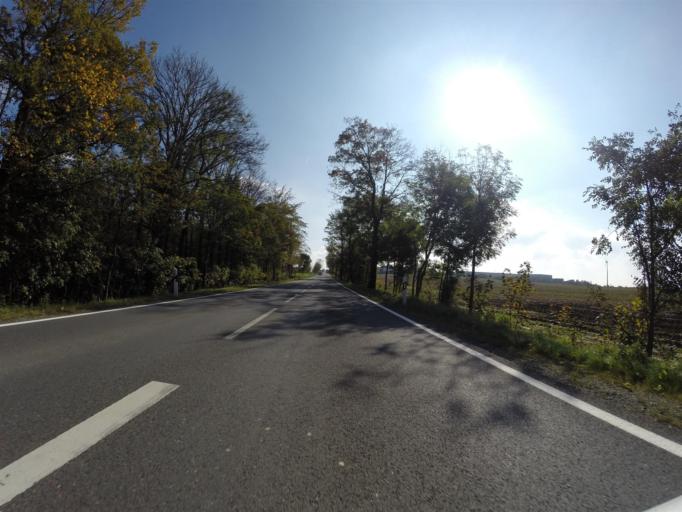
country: DE
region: Thuringia
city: Tanna
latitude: 50.5005
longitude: 11.8322
